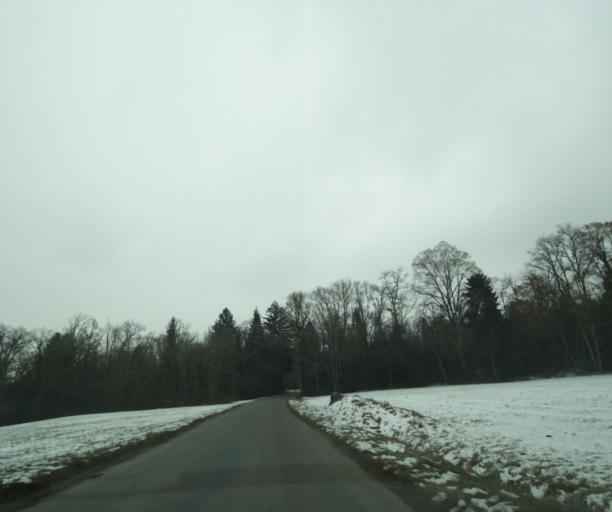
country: FR
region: Rhone-Alpes
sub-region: Departement de la Haute-Savoie
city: Cornier
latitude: 46.1184
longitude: 6.2910
